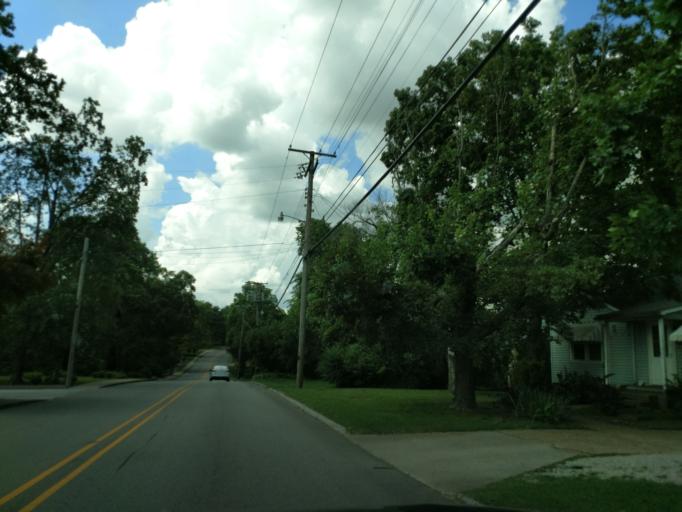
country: US
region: Arkansas
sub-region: Carroll County
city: Berryville
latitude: 36.3671
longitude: -93.5666
